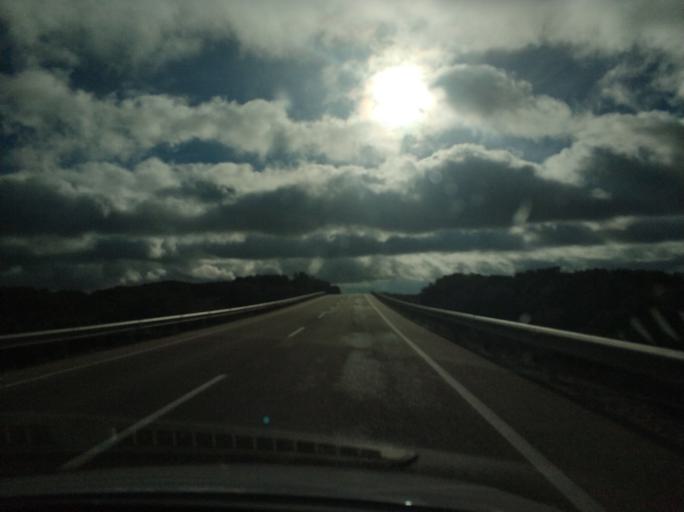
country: ES
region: Castille and Leon
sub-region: Provincia de Soria
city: Fuentecambron
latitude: 41.4925
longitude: -3.3116
